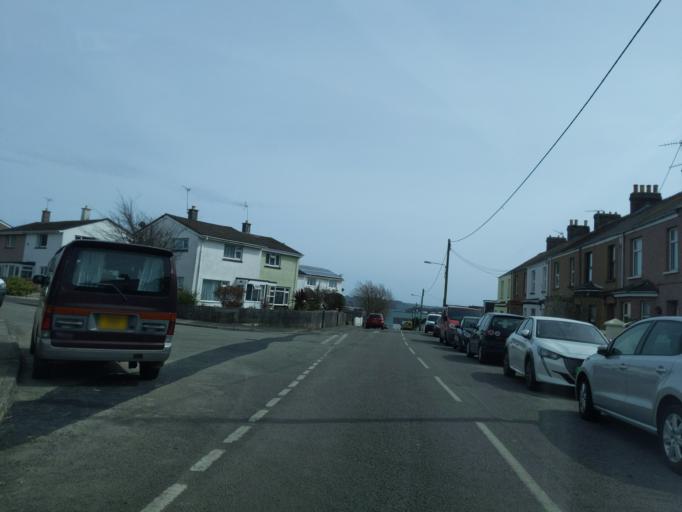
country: GB
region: England
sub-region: Cornwall
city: Torpoint
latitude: 50.3724
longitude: -4.2021
